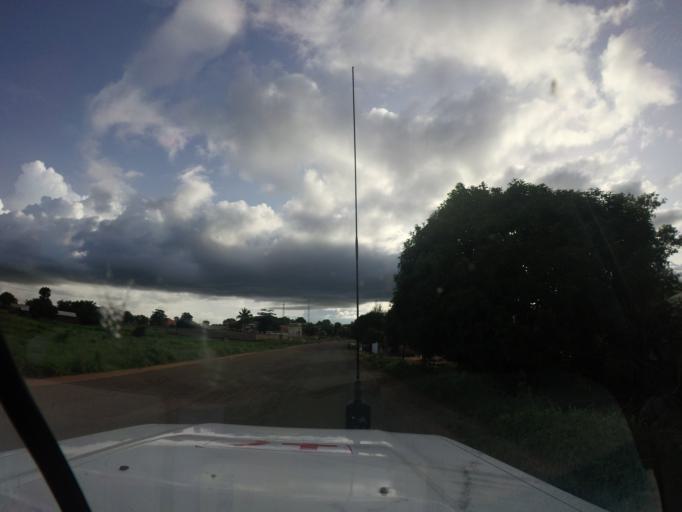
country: GN
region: Kindia
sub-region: Kindia
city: Kindia
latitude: 10.0172
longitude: -12.8853
